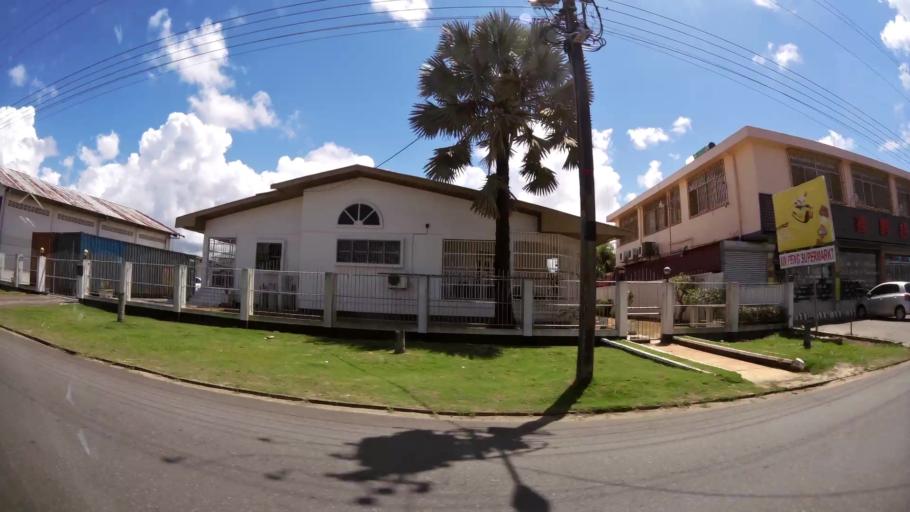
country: SR
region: Paramaribo
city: Paramaribo
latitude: 5.8575
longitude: -55.1448
